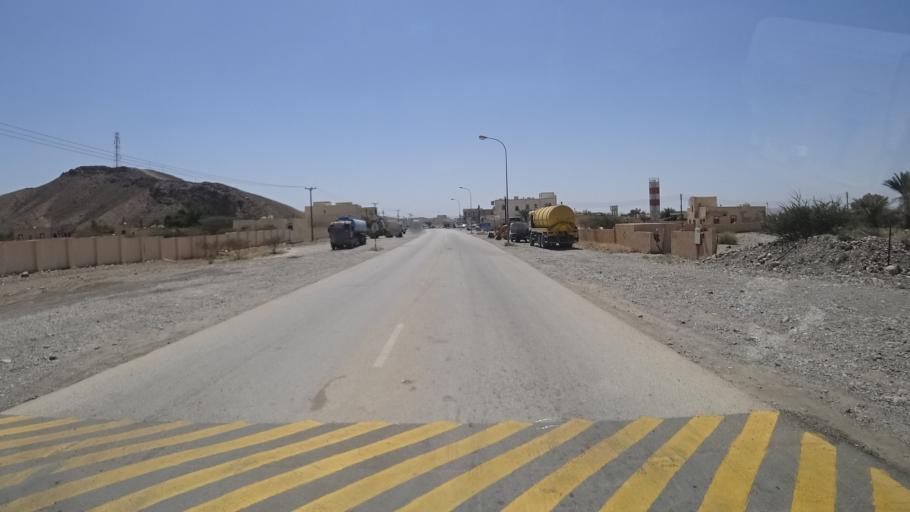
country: OM
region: Az Zahirah
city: `Ibri
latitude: 23.1351
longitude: 56.8913
